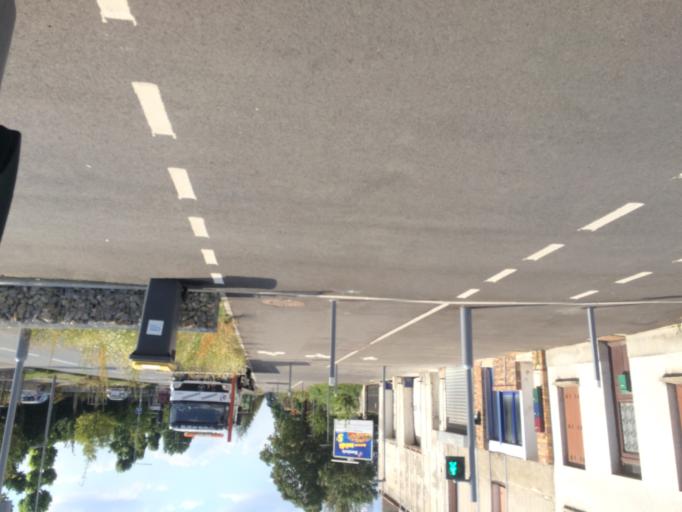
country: FR
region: Ile-de-France
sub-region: Departement de l'Essonne
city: Longjumeau
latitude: 48.7093
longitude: 2.2976
